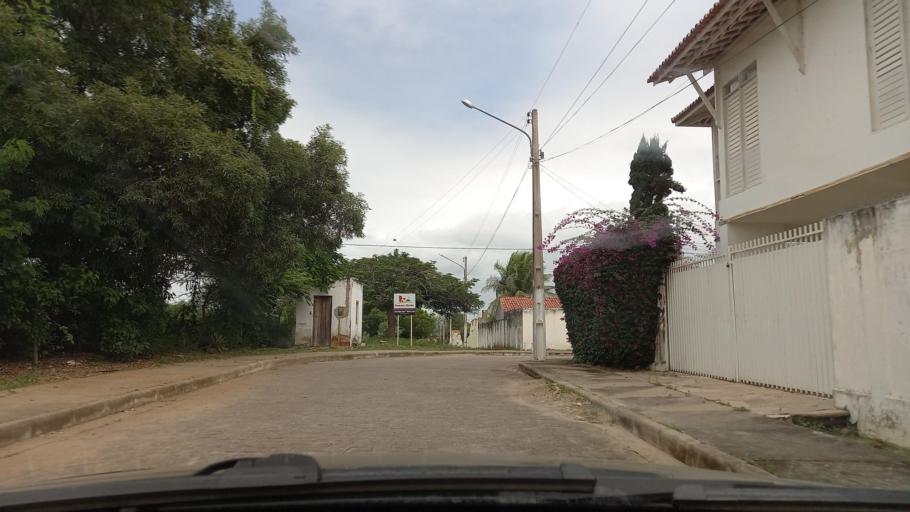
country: BR
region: Sergipe
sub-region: Caninde De Sao Francisco
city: Caninde de Sao Francisco
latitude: -9.6148
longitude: -37.7652
